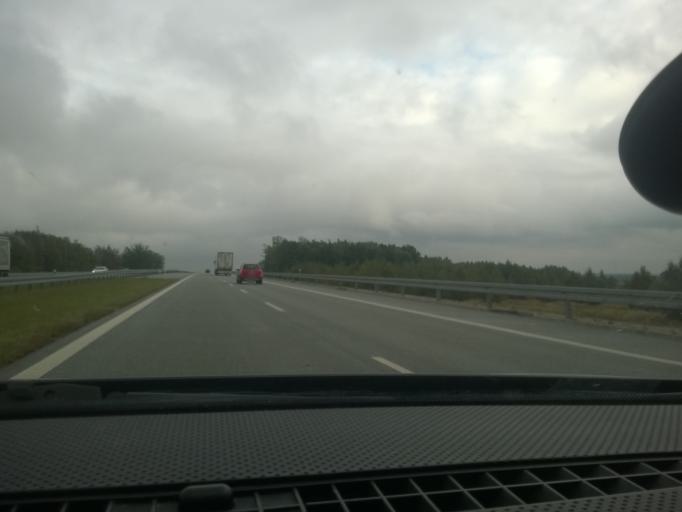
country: PL
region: Lodz Voivodeship
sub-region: Powiat zdunskowolski
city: Zdunska Wola
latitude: 51.5669
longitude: 18.9802
